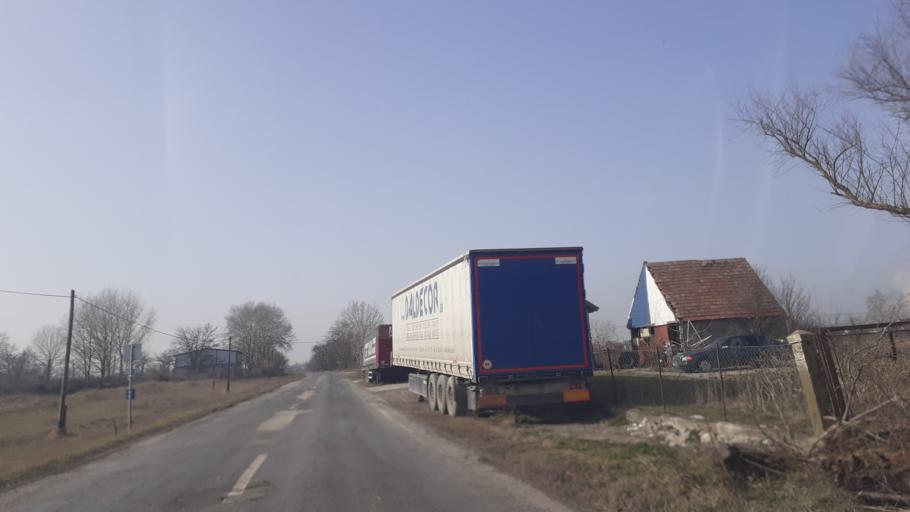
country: HU
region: Bacs-Kiskun
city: Kunszentmiklos
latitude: 47.0262
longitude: 19.1517
